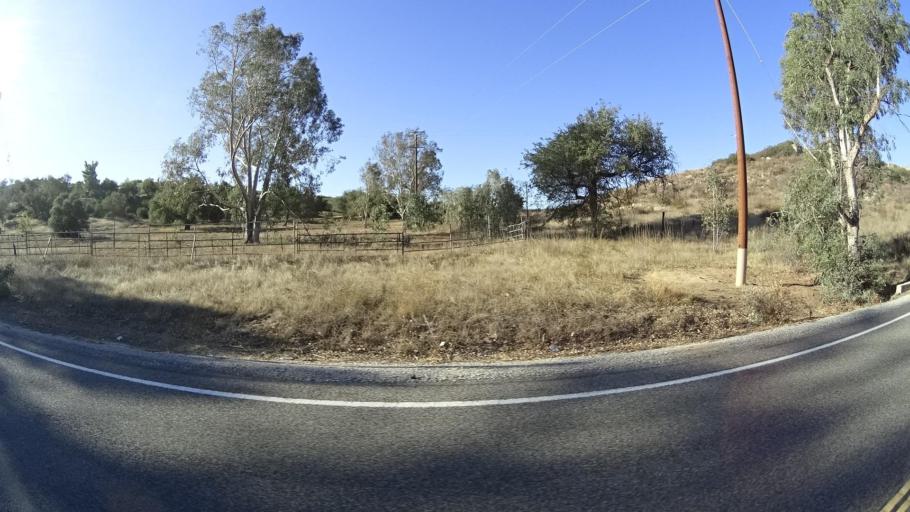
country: MX
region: Baja California
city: Tecate
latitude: 32.6079
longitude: -116.6245
